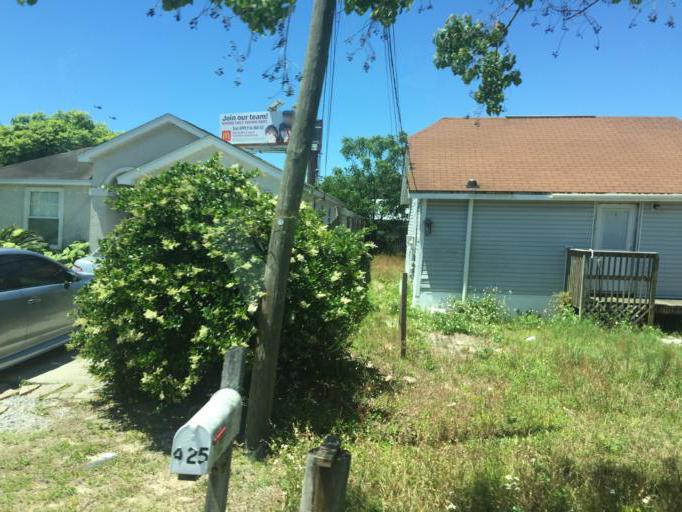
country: US
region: Florida
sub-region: Bay County
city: Laguna Beach
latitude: 30.2644
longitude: -85.9681
